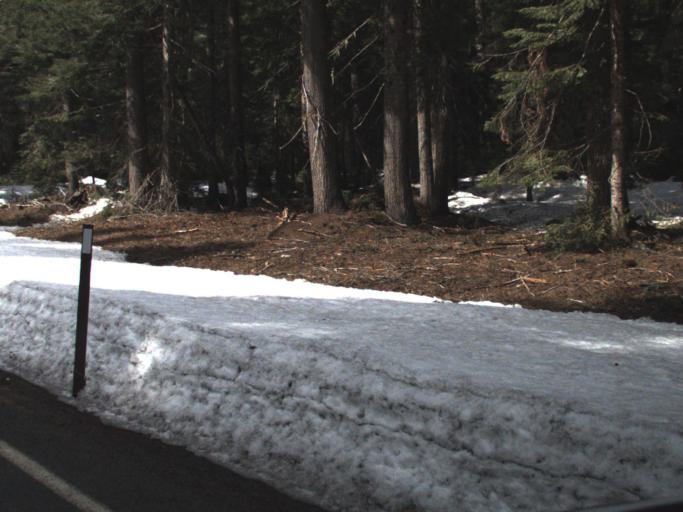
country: US
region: Washington
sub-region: Kittitas County
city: Cle Elum
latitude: 46.9616
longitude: -121.2776
